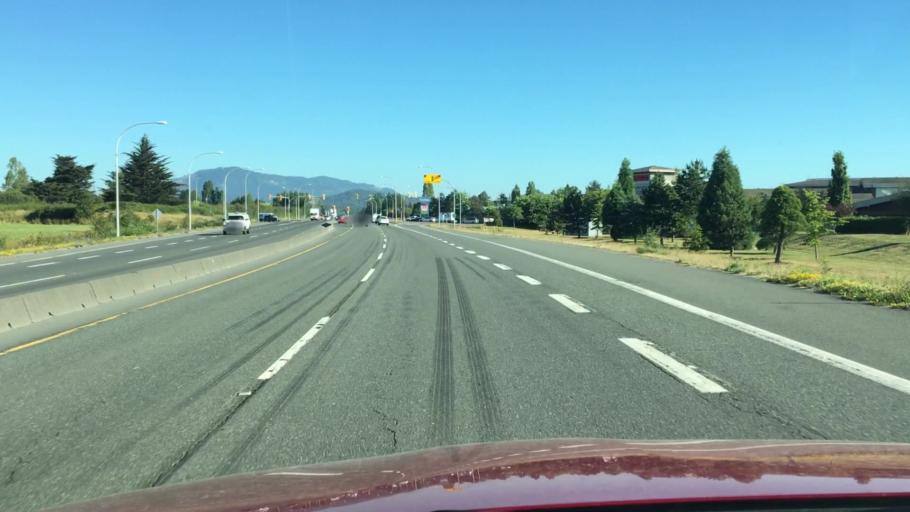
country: CA
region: British Columbia
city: North Saanich
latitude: 48.6469
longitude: -123.4056
